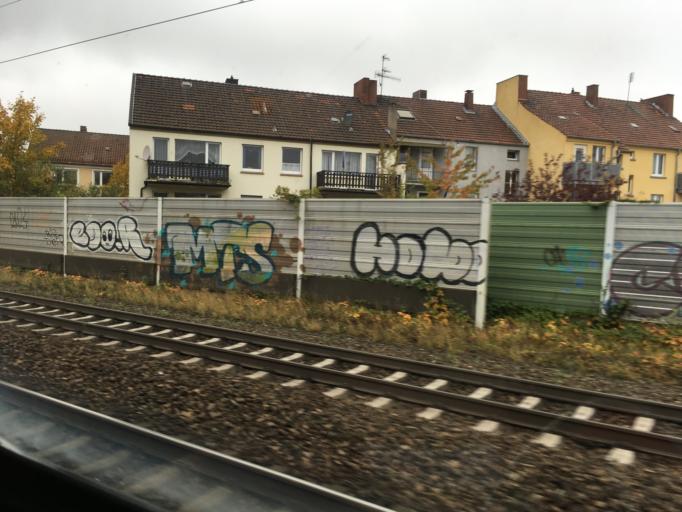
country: DE
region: Lower Saxony
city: Osnabrueck
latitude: 52.2635
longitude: 8.0503
